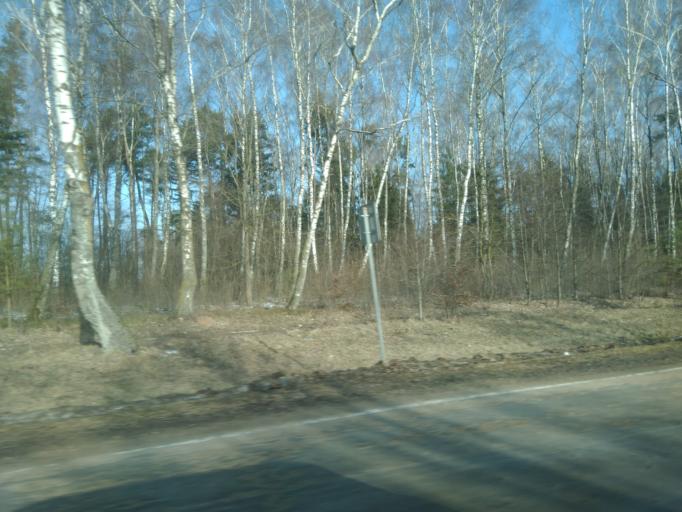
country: BY
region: Minsk
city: Snow
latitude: 53.2160
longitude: 26.4399
